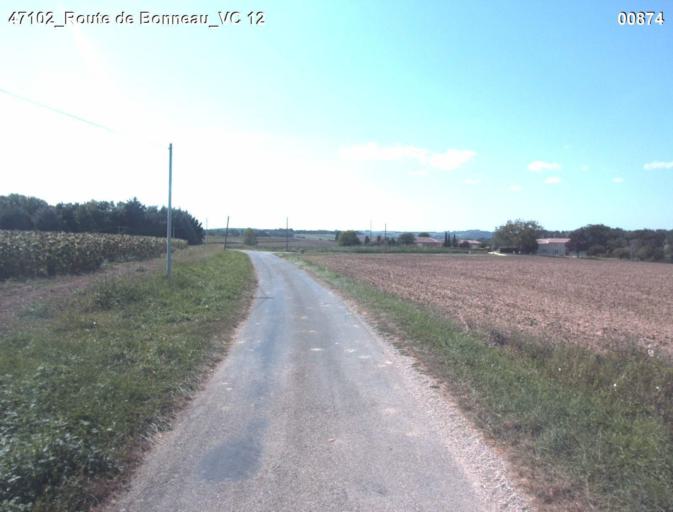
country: FR
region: Aquitaine
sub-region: Departement du Lot-et-Garonne
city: Nerac
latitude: 44.0830
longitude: 0.4073
